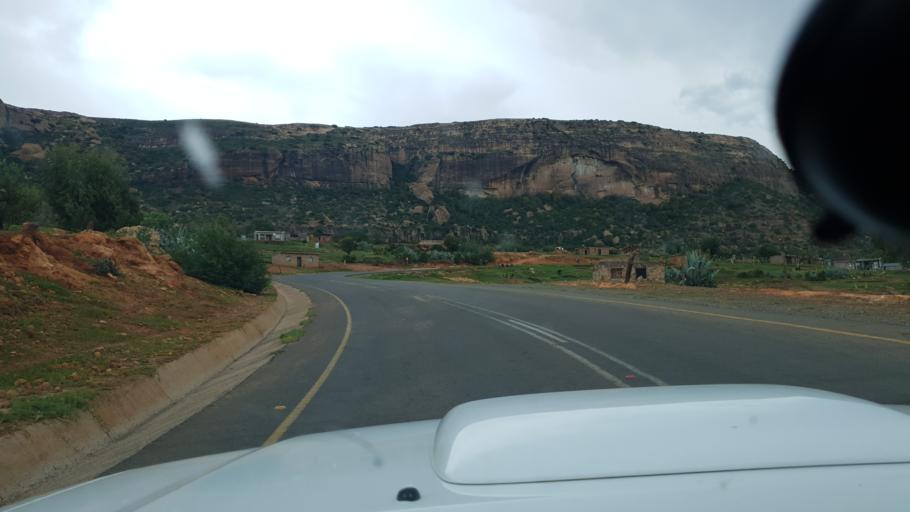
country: LS
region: Maseru
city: Maseru
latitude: -29.4587
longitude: 27.4890
